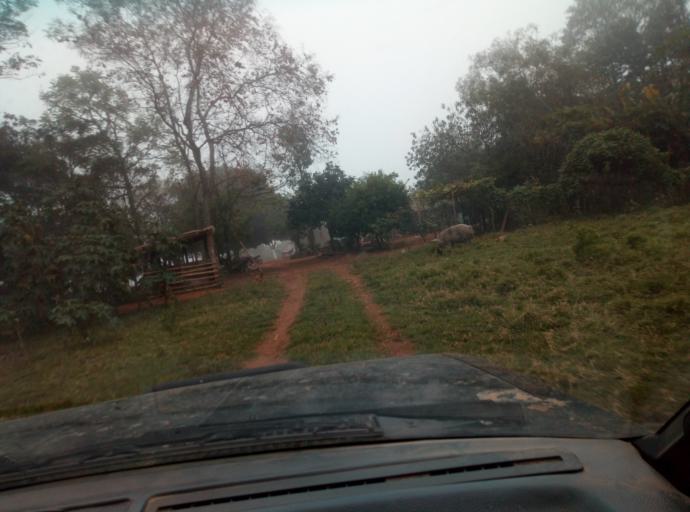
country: PY
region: Caaguazu
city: Doctor Cecilio Baez
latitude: -25.1548
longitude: -56.2502
